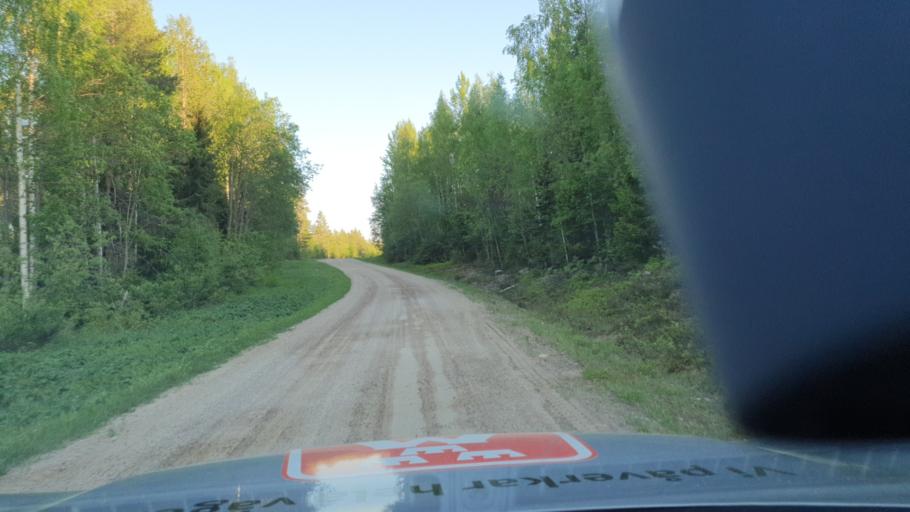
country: FI
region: Lapland
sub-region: Torniolaakso
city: Ylitornio
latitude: 66.1069
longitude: 23.7176
